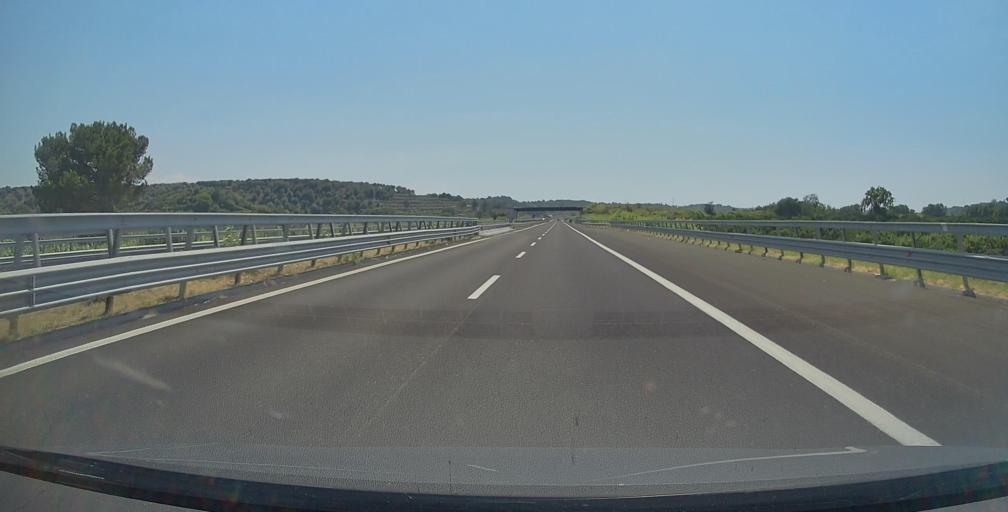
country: IT
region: Calabria
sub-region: Provincia di Reggio Calabria
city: Candidoni
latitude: 38.5061
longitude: 16.0387
